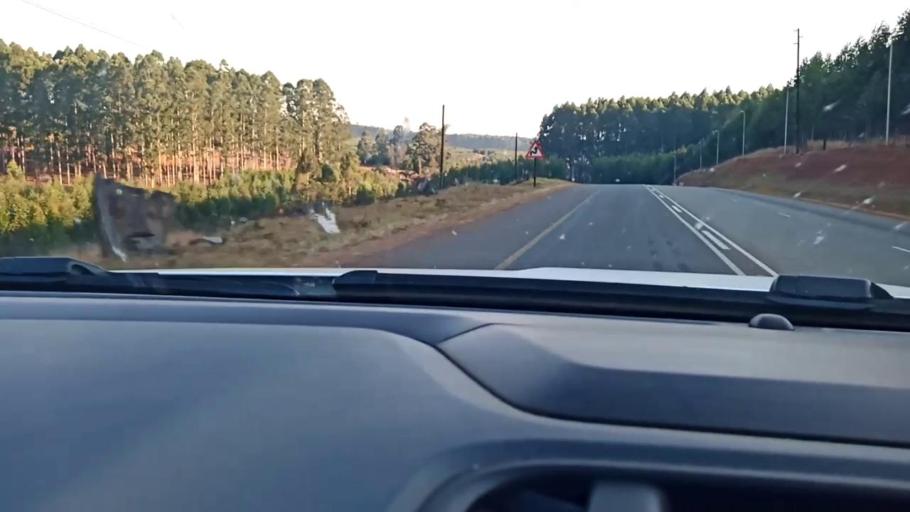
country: ZA
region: Limpopo
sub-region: Mopani District Municipality
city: Duiwelskloof
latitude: -23.7060
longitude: 30.1319
